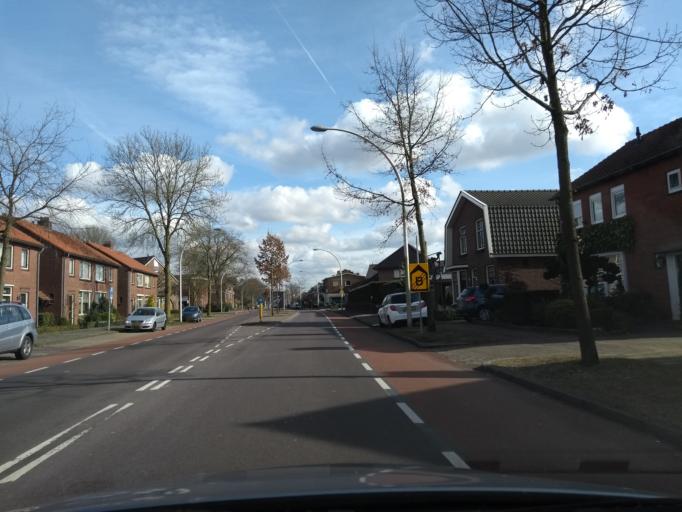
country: NL
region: Overijssel
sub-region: Gemeente Hengelo
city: Hengelo
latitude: 52.2535
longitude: 6.7773
